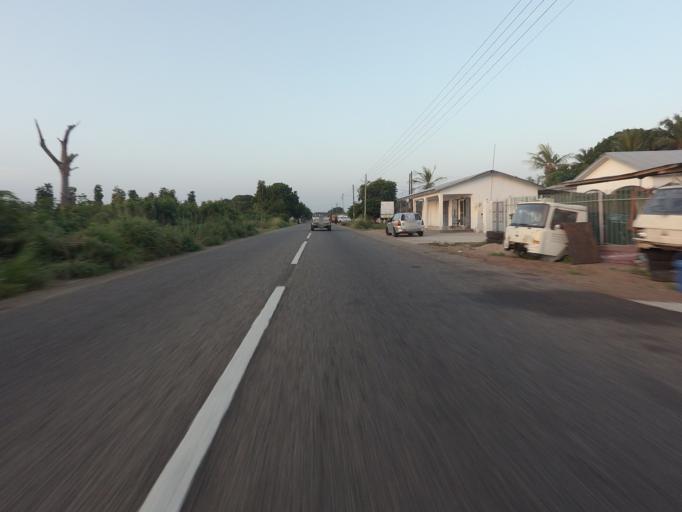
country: GH
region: Volta
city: Anloga
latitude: 5.8207
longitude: 0.9445
